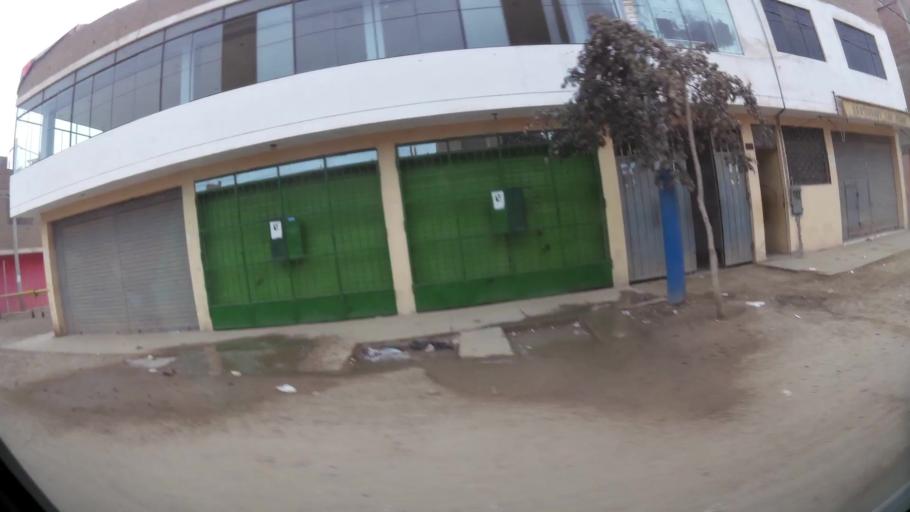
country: PE
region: Lima
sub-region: Lima
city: Independencia
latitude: -11.9602
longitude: -77.0981
